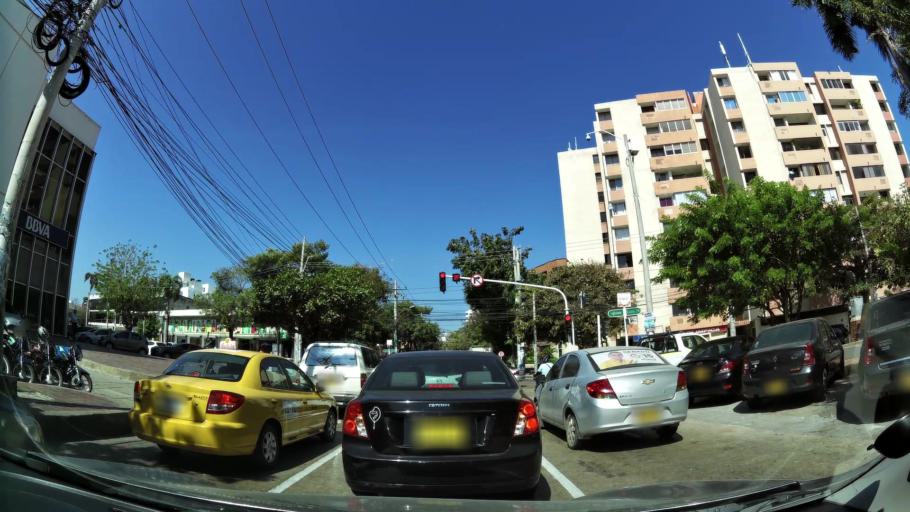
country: CO
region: Atlantico
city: Barranquilla
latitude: 10.9971
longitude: -74.8005
